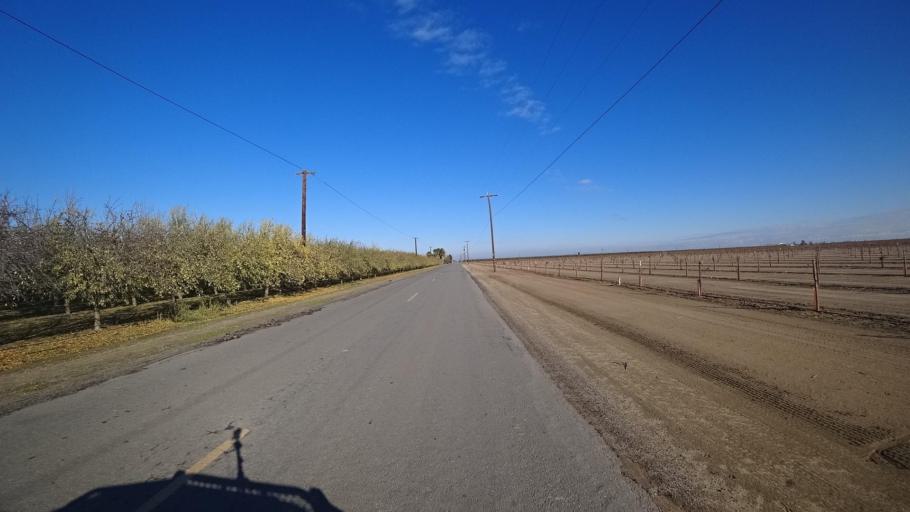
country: US
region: California
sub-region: Kern County
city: Delano
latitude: 35.7119
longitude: -119.3119
